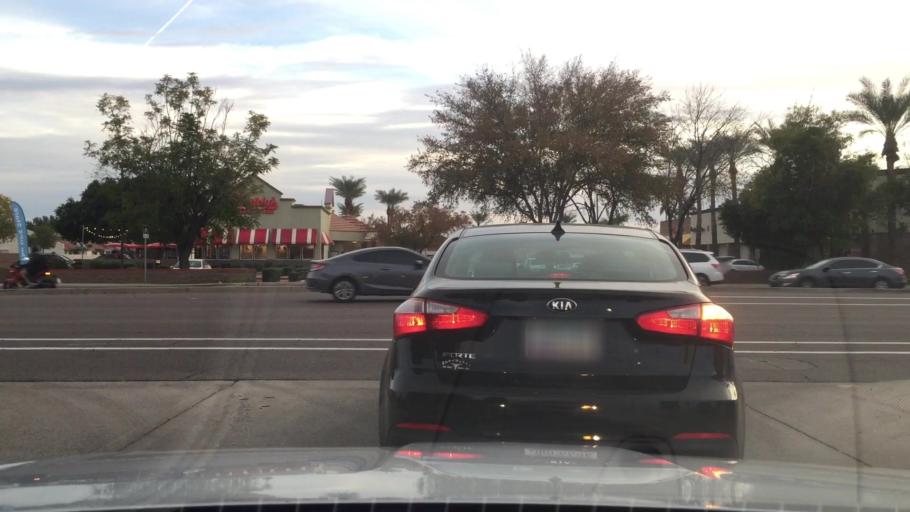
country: US
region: Arizona
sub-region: Maricopa County
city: Gilbert
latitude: 33.3793
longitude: -111.7874
